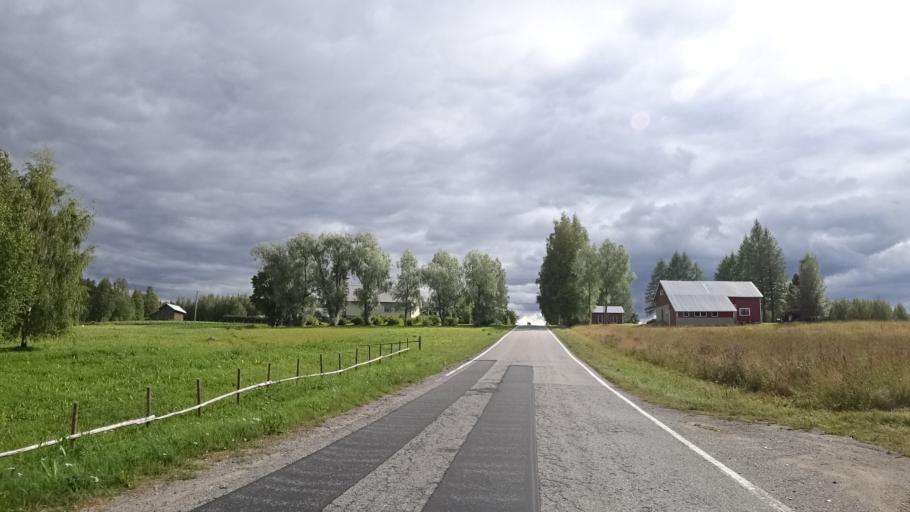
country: FI
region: North Karelia
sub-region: Joensuu
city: Ilomantsi
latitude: 62.4515
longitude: 31.1149
